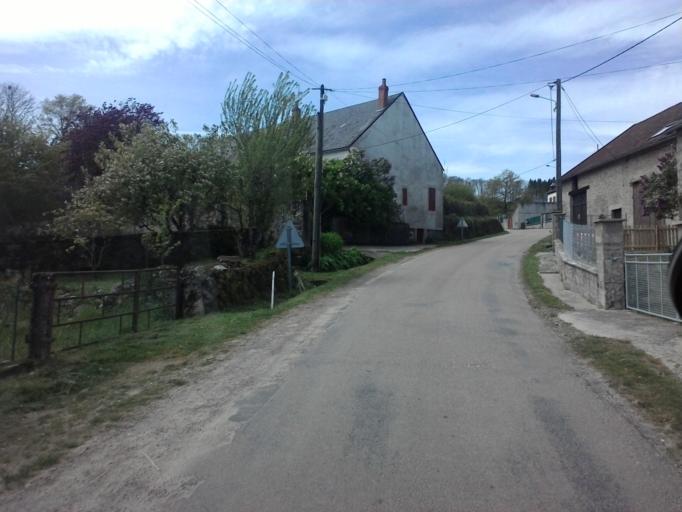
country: FR
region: Bourgogne
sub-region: Departement de la Nievre
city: Lormes
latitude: 47.3022
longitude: 3.8983
